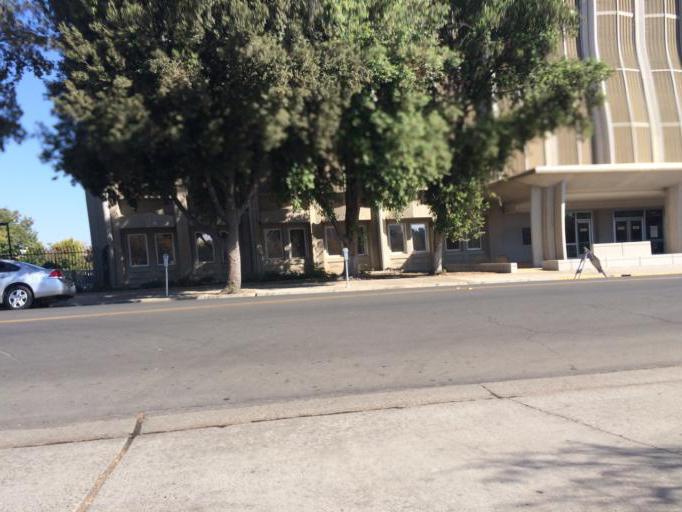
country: US
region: California
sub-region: Fresno County
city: Fresno
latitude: 36.7391
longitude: -119.7869
